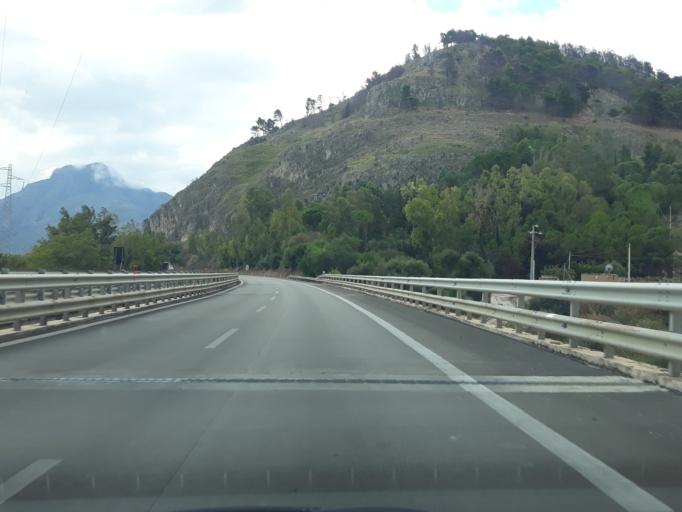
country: IT
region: Sicily
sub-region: Palermo
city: Trabia
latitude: 37.9858
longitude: 13.6569
